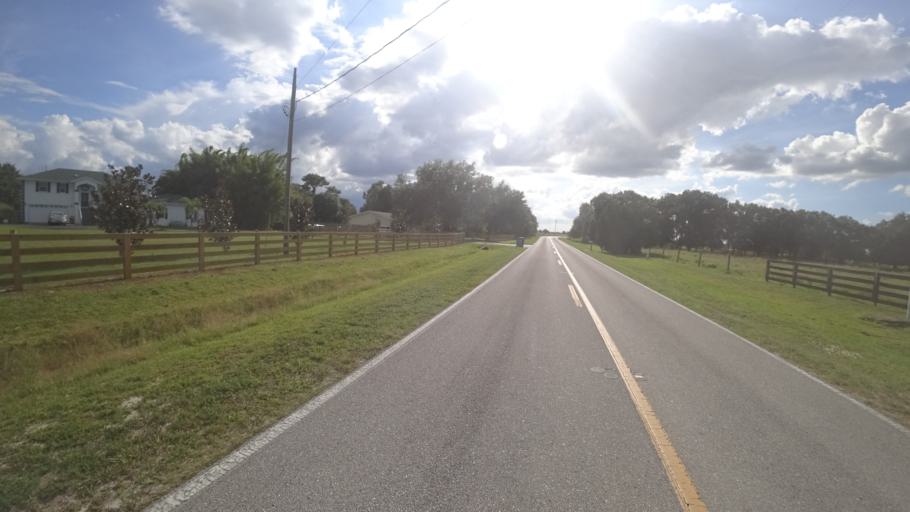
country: US
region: Florida
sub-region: Sarasota County
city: Lake Sarasota
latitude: 27.3401
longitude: -82.1748
